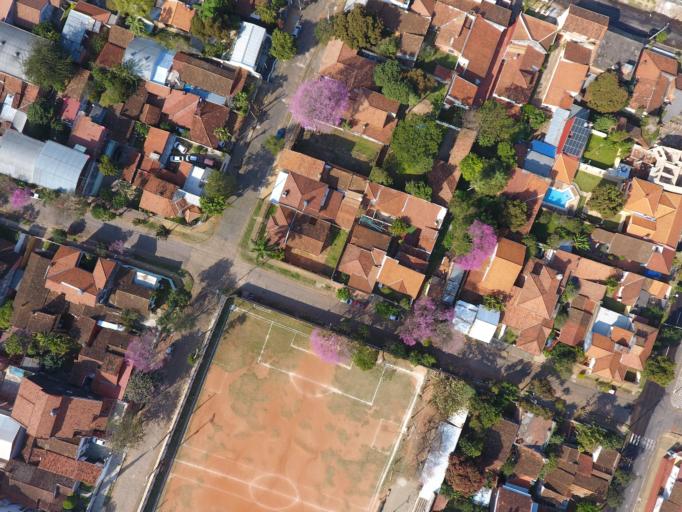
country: PY
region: Asuncion
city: Asuncion
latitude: -25.3097
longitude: -57.6065
